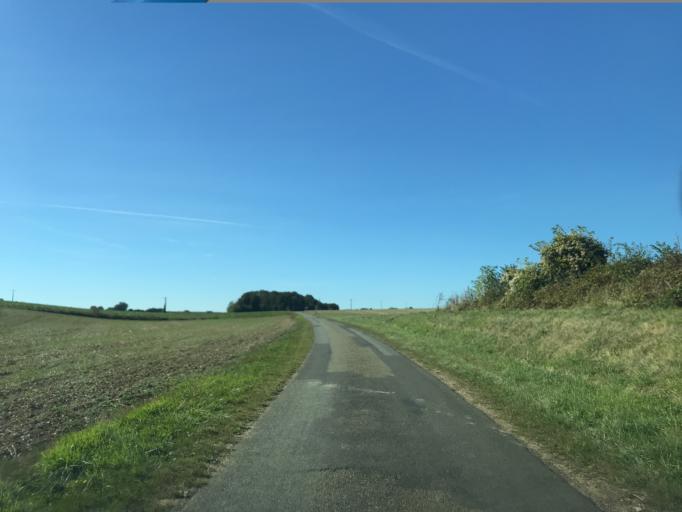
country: FR
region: Haute-Normandie
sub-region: Departement de l'Eure
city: Ande
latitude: 49.1746
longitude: 1.2632
